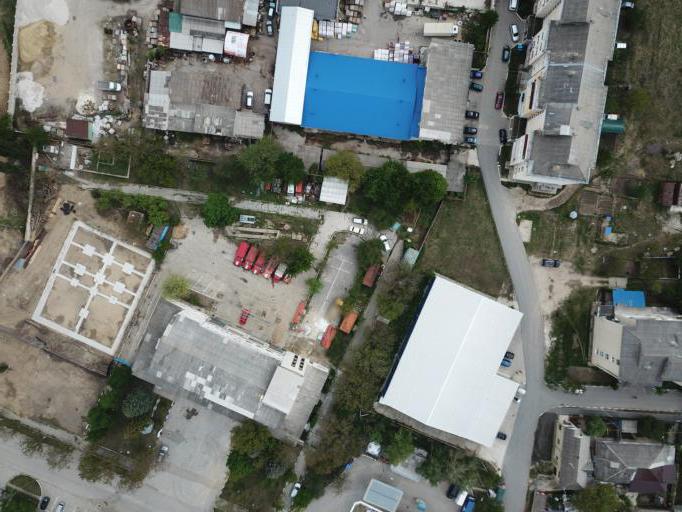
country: MD
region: Ungheni
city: Ungheni
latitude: 47.2190
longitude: 27.8064
